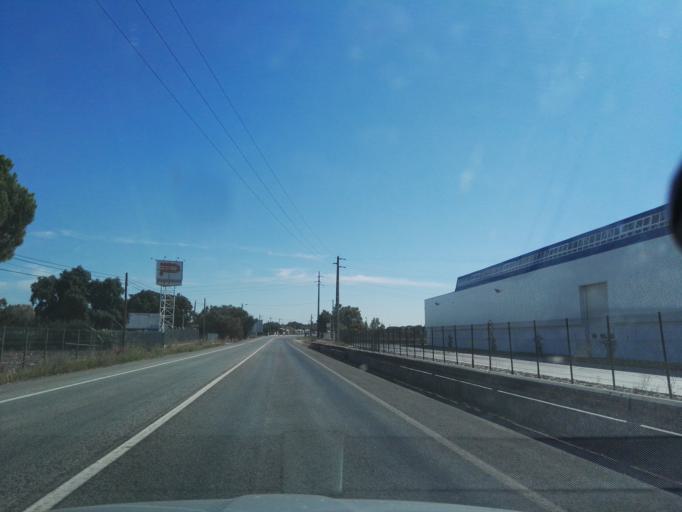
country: PT
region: Santarem
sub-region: Benavente
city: Samora Correia
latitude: 38.9122
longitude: -8.8524
